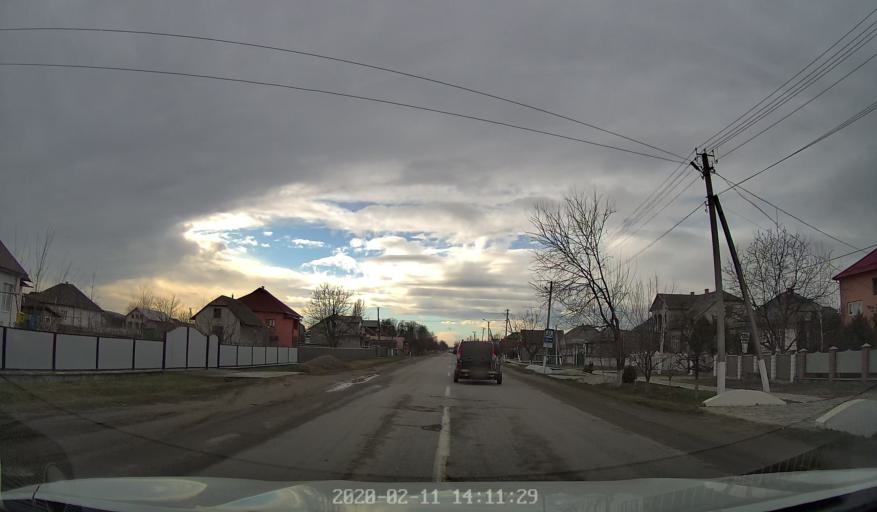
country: RO
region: Botosani
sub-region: Comuna Darabani
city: Bajura
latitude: 48.2241
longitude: 26.5058
